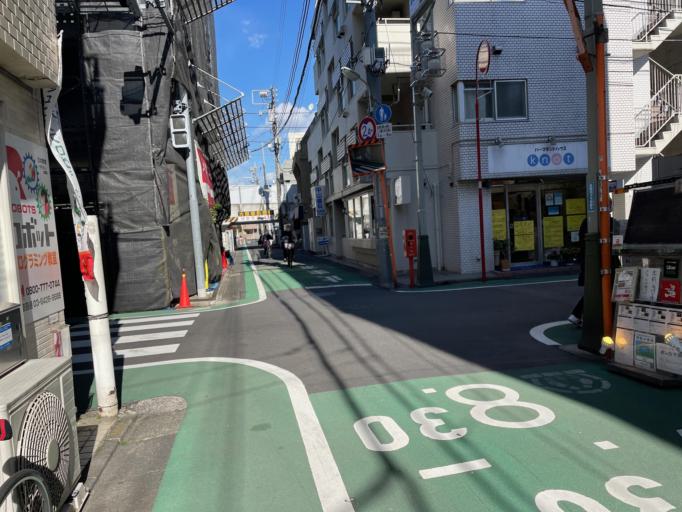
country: JP
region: Kanagawa
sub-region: Kawasaki-shi
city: Kawasaki
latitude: 35.6039
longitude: 139.7049
